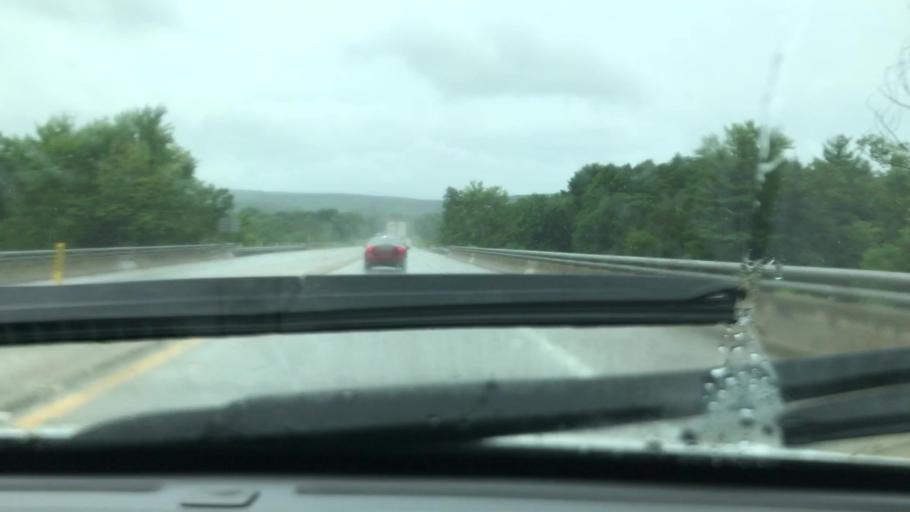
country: US
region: Pennsylvania
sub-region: Blair County
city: Tyrone
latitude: 40.7128
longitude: -78.1879
